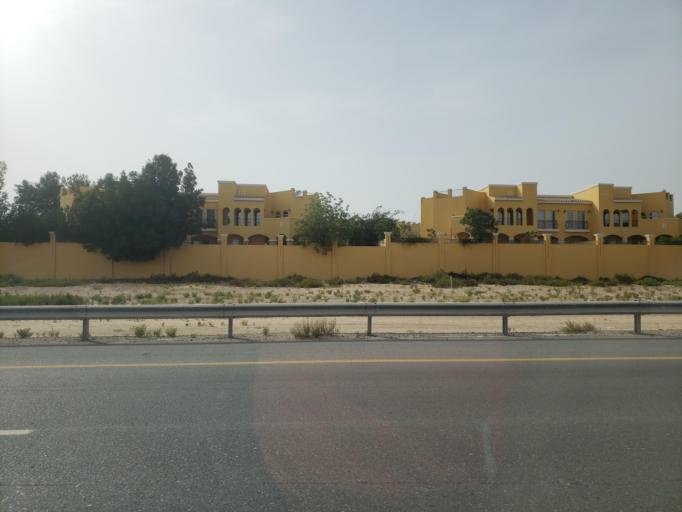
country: AE
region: Dubai
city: Dubai
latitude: 25.0289
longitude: 55.2878
